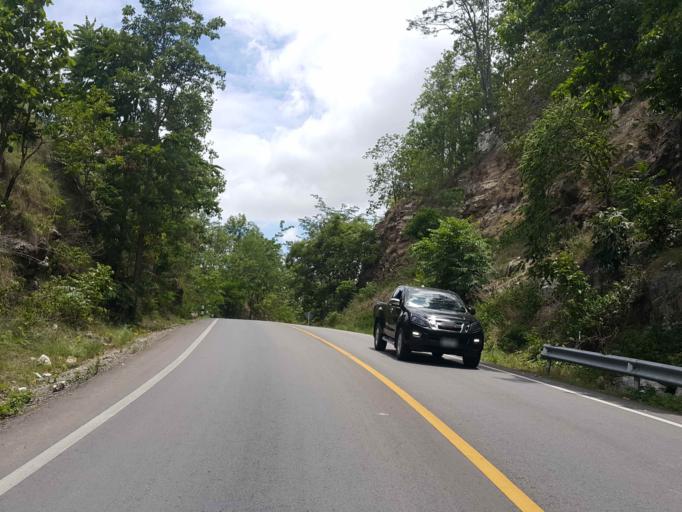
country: TH
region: Chiang Mai
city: Chom Thong
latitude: 18.5007
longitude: 98.6706
